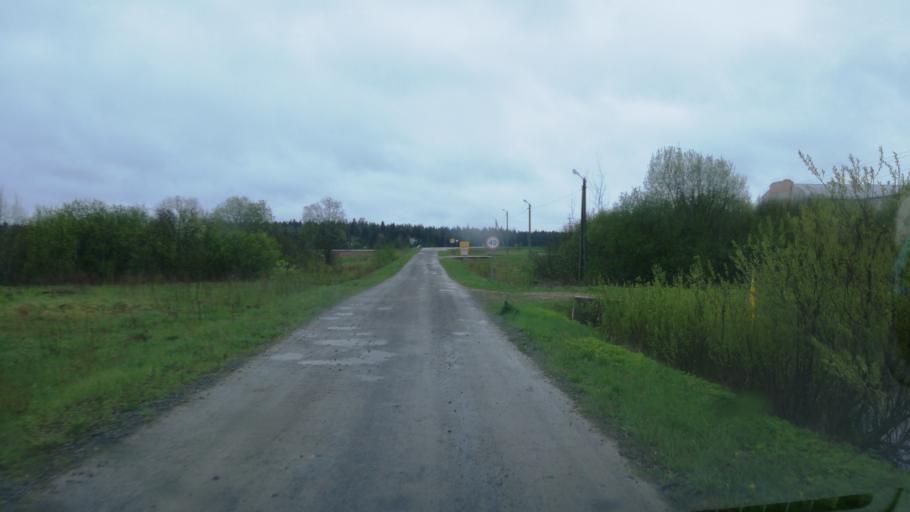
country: RU
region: Jaroslavl
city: Danilov
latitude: 57.9928
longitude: 40.1811
